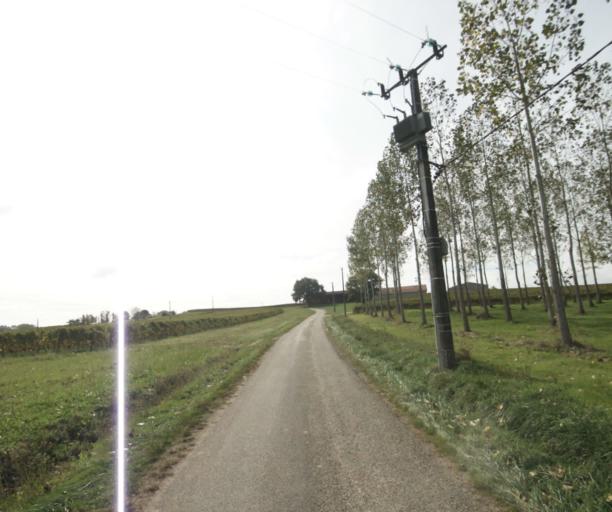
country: FR
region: Midi-Pyrenees
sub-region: Departement du Gers
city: Eauze
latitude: 43.8495
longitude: 0.1399
